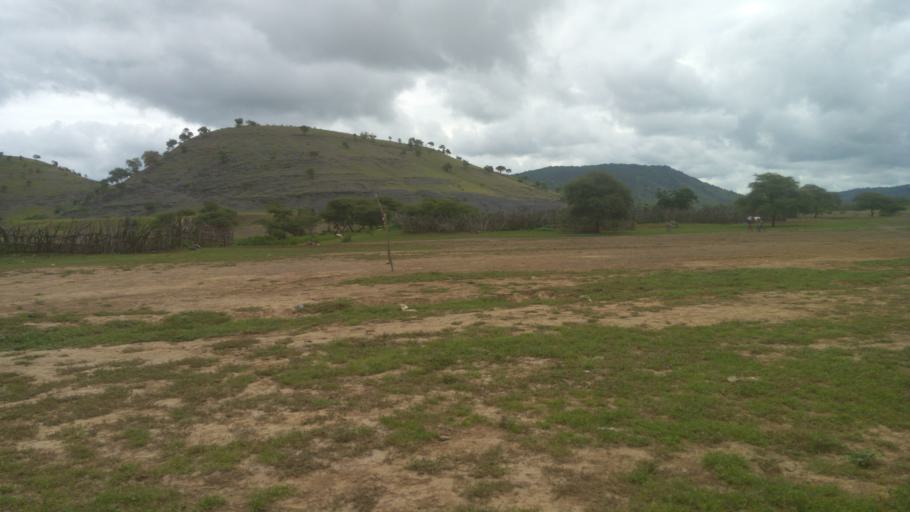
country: ML
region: Kayes
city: Yelimane
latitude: 14.6460
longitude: -10.6965
